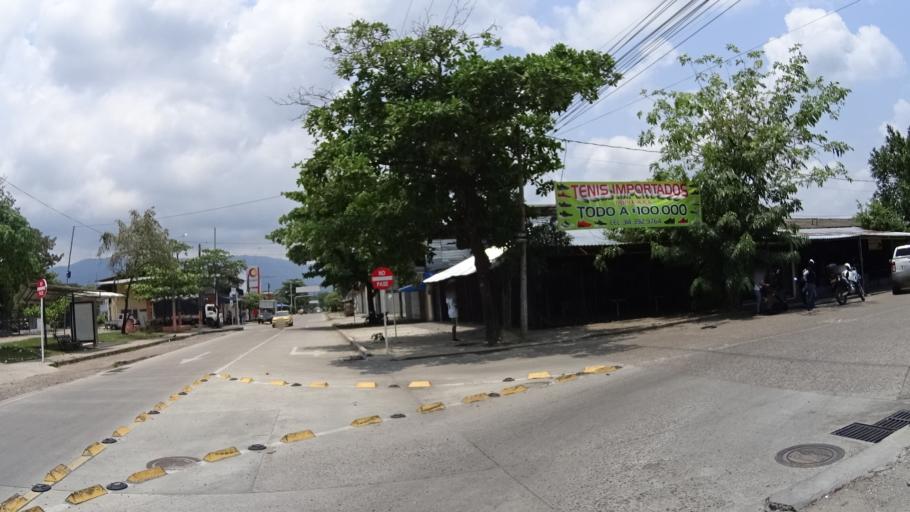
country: CO
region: Cundinamarca
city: Puerto Salgar
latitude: 5.4604
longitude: -74.6649
